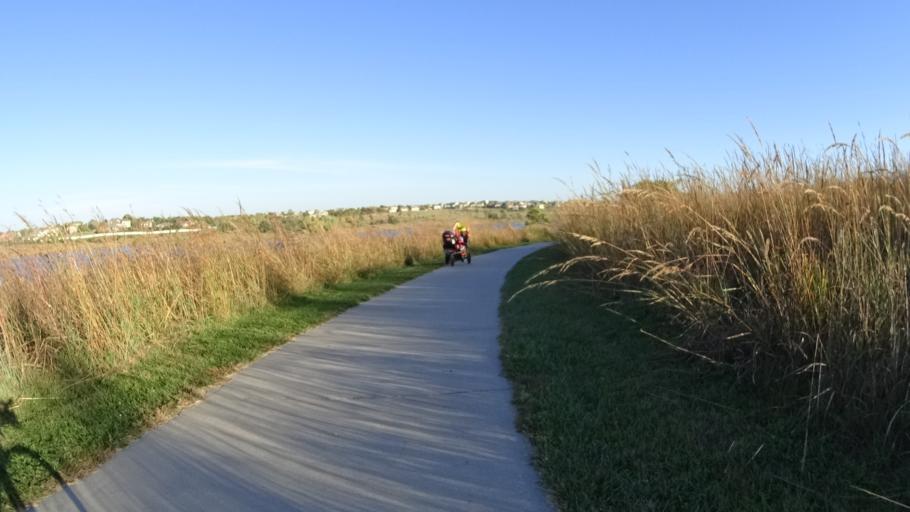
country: US
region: Nebraska
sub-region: Sarpy County
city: Papillion
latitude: 41.1414
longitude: -96.0719
